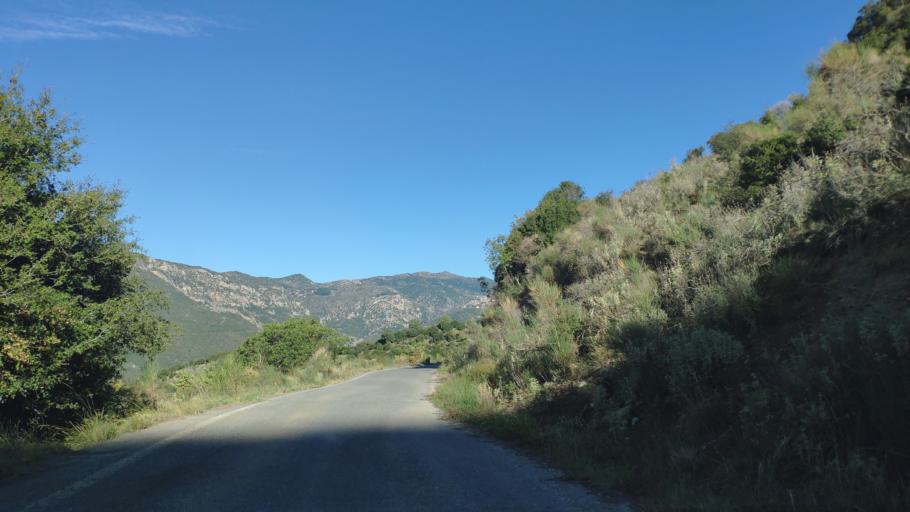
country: GR
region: Peloponnese
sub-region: Nomos Arkadias
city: Dimitsana
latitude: 37.5544
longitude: 22.0607
